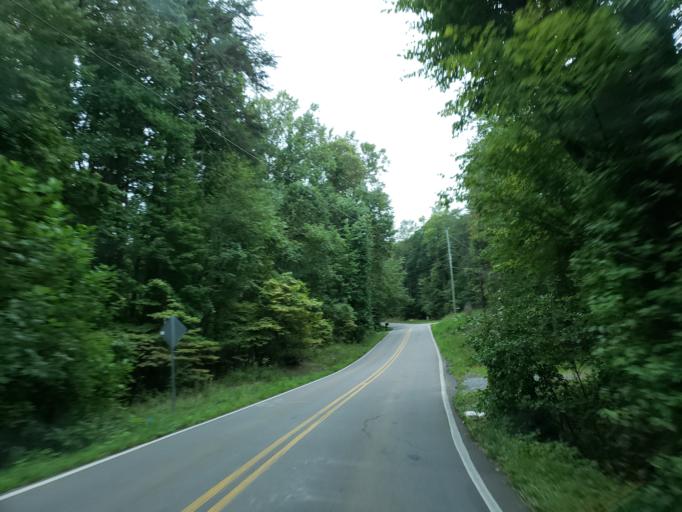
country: US
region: Georgia
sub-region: Pickens County
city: Jasper
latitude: 34.4213
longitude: -84.5399
